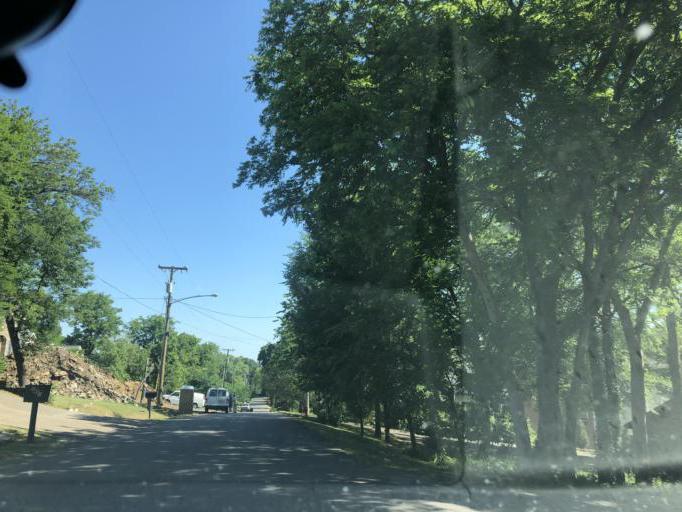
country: US
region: Tennessee
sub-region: Davidson County
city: Oak Hill
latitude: 36.1143
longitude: -86.8061
